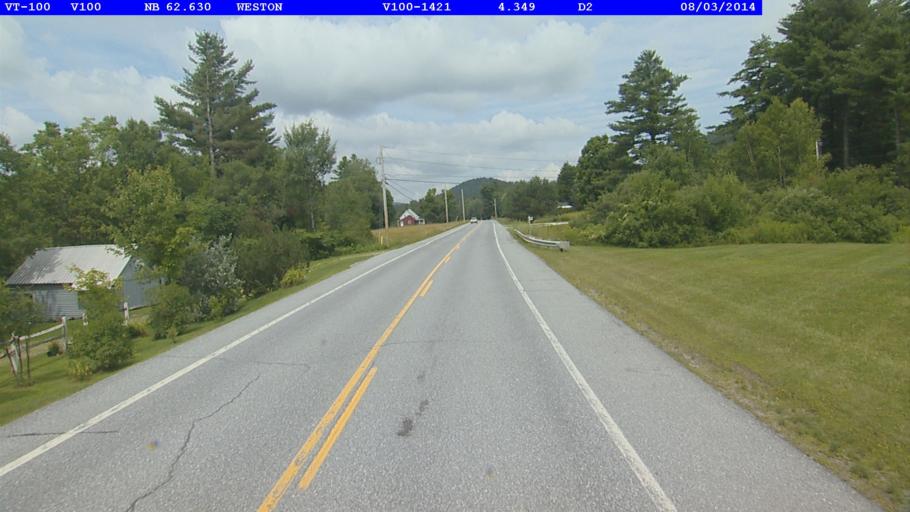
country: US
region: Vermont
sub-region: Windsor County
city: Chester
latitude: 43.3069
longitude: -72.7866
